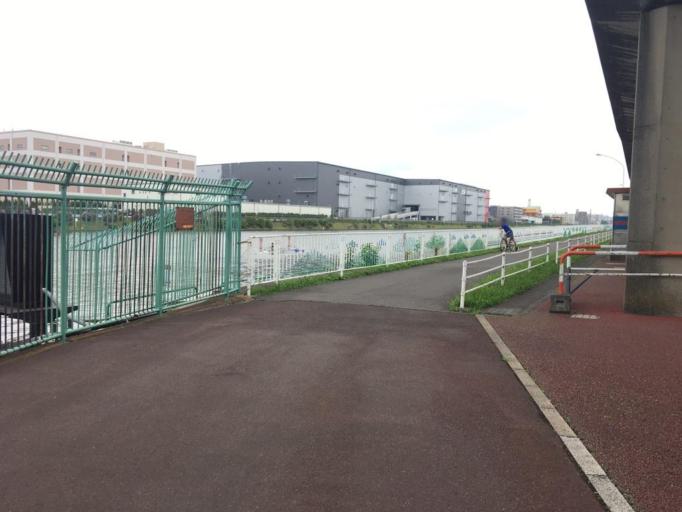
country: JP
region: Saitama
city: Shimotoda
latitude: 35.8032
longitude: 139.6608
